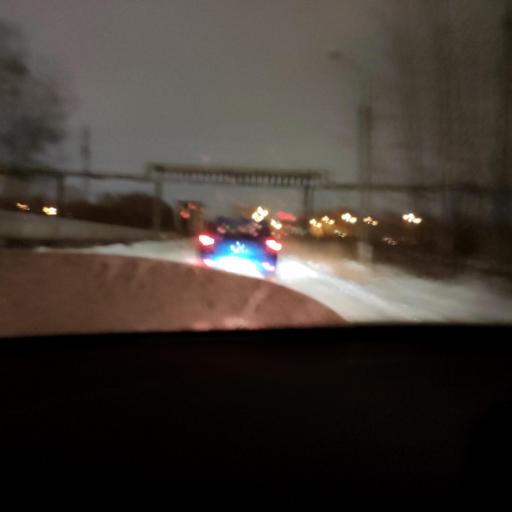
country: RU
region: Tatarstan
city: Staroye Arakchino
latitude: 55.8609
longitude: 48.9844
